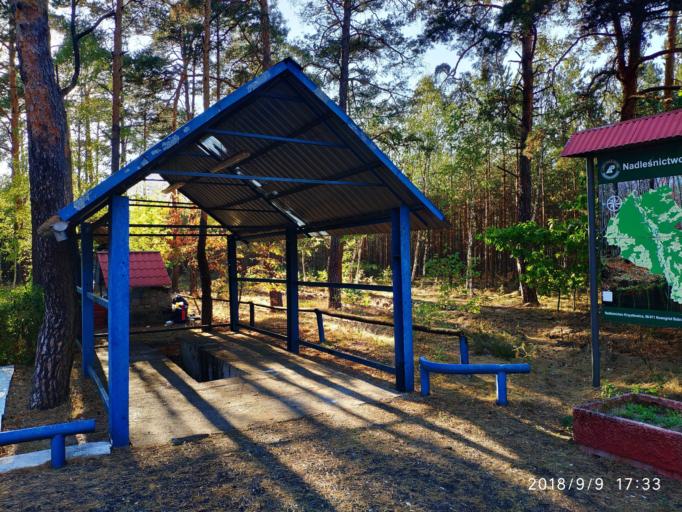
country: PL
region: Lubusz
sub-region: Powiat zielonogorski
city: Nowogrod Bobrzanski
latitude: 51.8237
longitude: 15.2992
